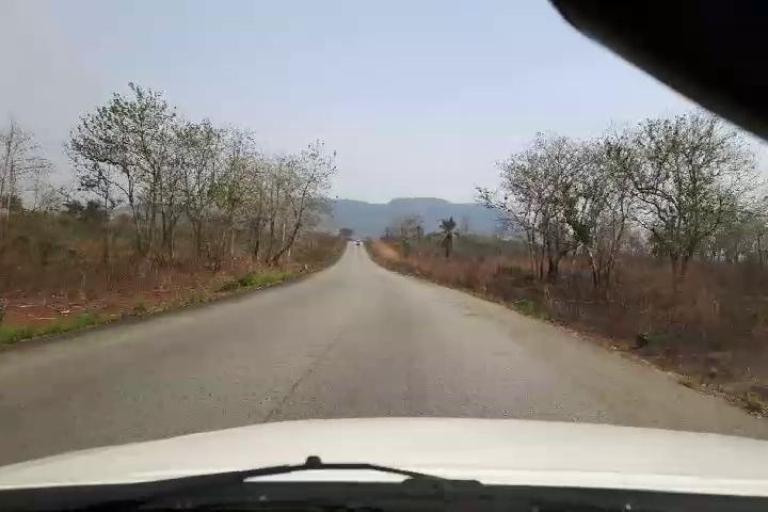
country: SL
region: Northern Province
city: Yonibana
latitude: 8.3932
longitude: -12.1932
